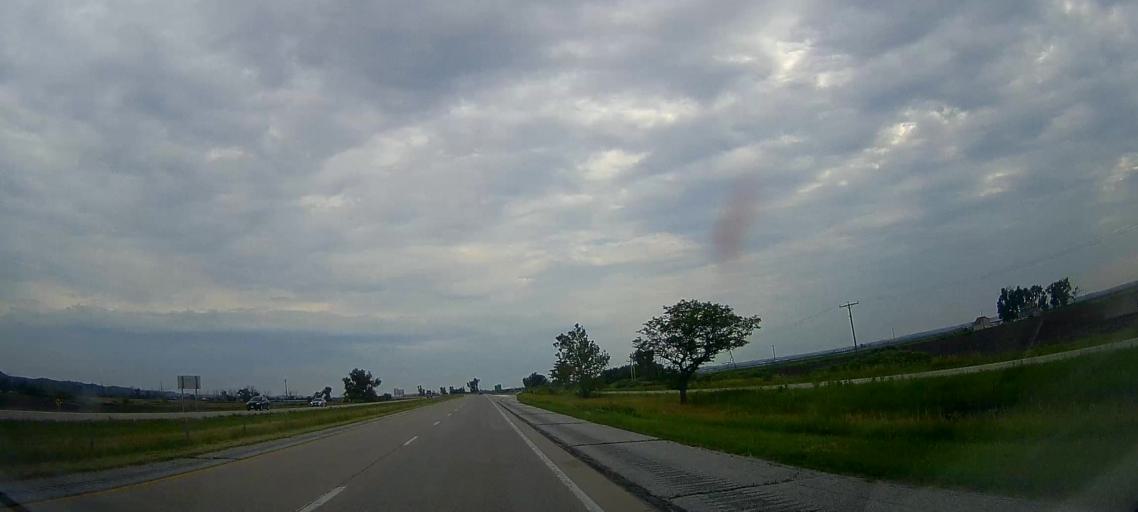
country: US
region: Iowa
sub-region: Harrison County
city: Missouri Valley
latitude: 41.5230
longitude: -95.9180
